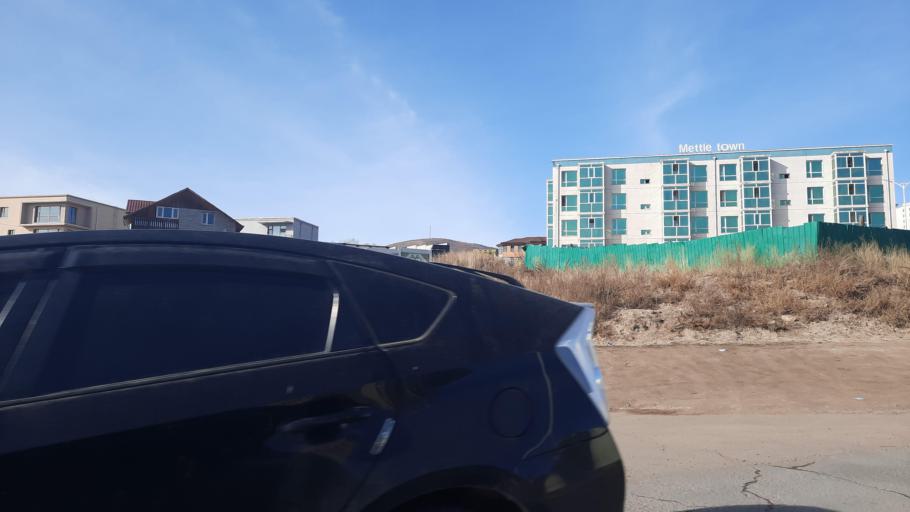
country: MN
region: Orhon
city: Erdenet
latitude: 49.0371
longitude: 104.0517
